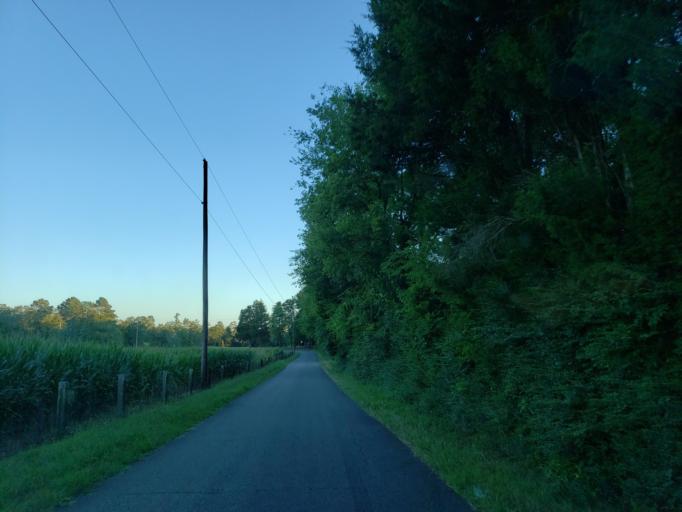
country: US
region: Georgia
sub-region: Bartow County
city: Euharlee
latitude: 34.1111
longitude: -84.8827
